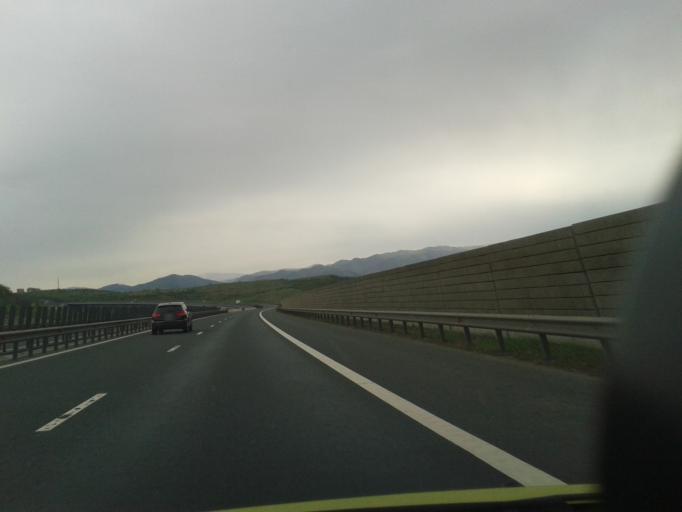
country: RO
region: Sibiu
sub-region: Comuna Orlat
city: Orlat
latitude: 45.7882
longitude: 23.9450
